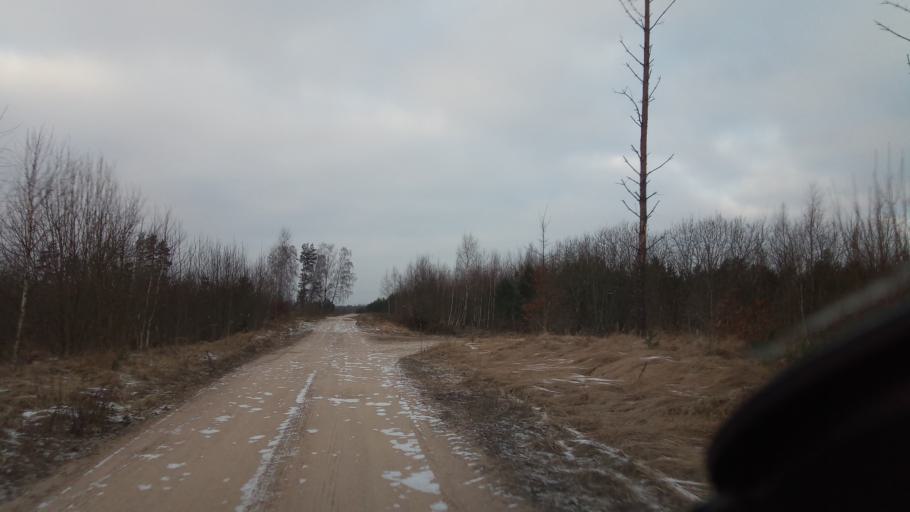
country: LT
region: Alytaus apskritis
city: Varena
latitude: 54.3700
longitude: 24.5413
